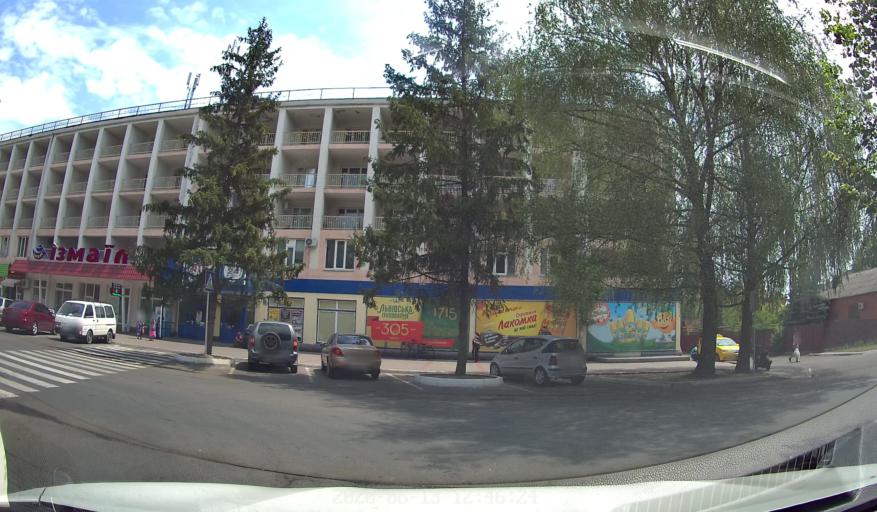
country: GR
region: East Macedonia and Thrace
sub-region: Nomos Evrou
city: Alexandroupoli
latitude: 40.8100
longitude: 25.9489
